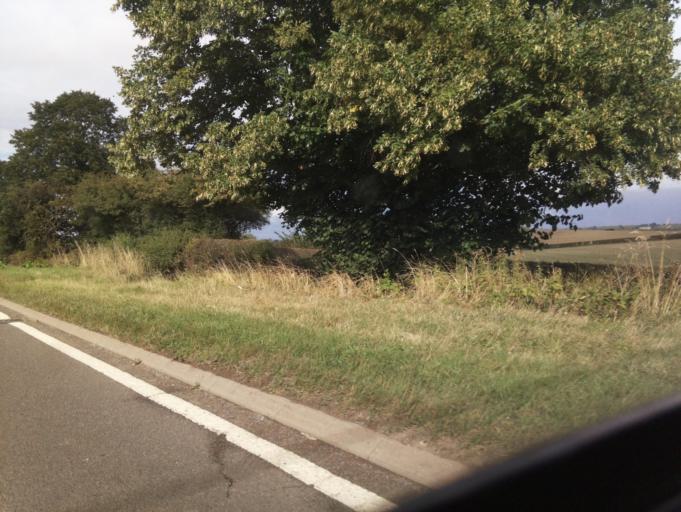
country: GB
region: England
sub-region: Shropshire
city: Ryton
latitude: 52.5913
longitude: -2.3984
